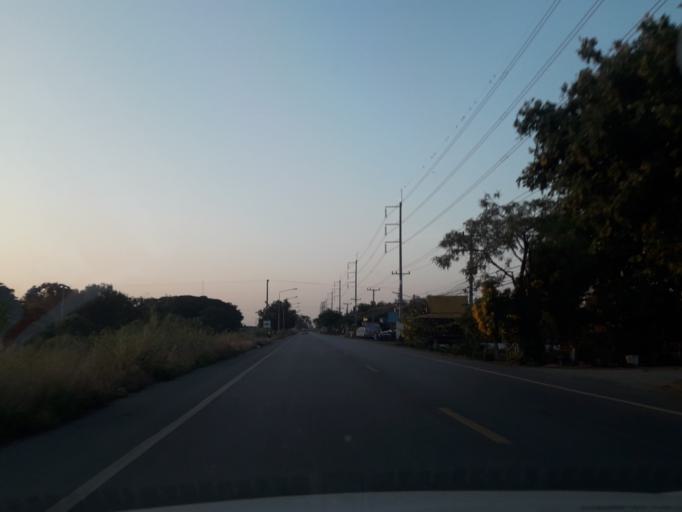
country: TH
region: Phra Nakhon Si Ayutthaya
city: Bang Pahan
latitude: 14.4873
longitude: 100.5561
